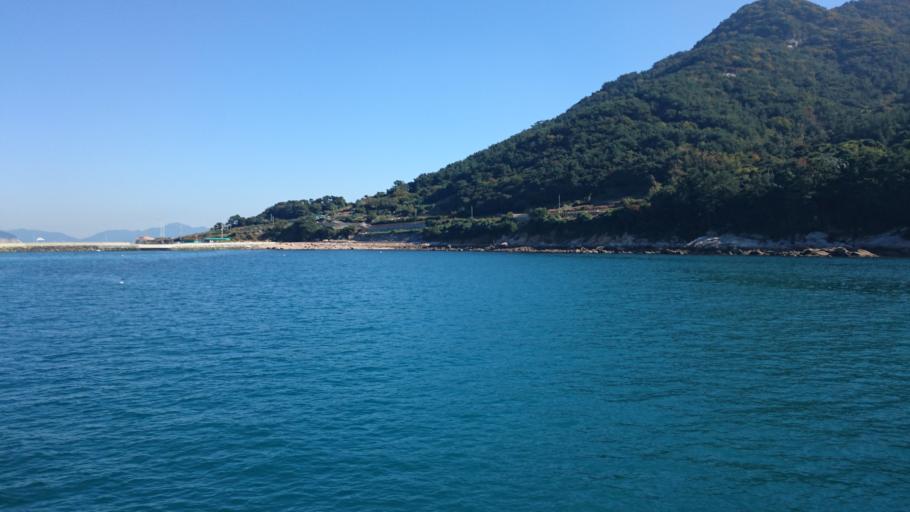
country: KR
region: Gyeongsangnam-do
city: Kyosai
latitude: 34.7168
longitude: 128.4537
